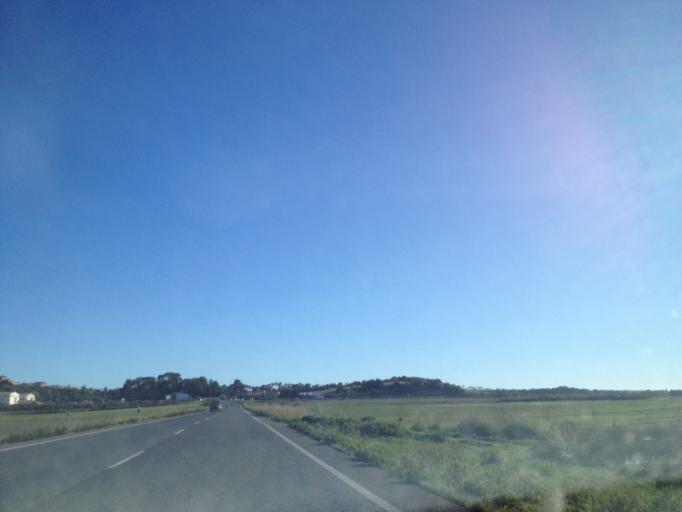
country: ES
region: Balearic Islands
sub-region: Illes Balears
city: Ariany
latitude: 39.6459
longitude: 3.0931
